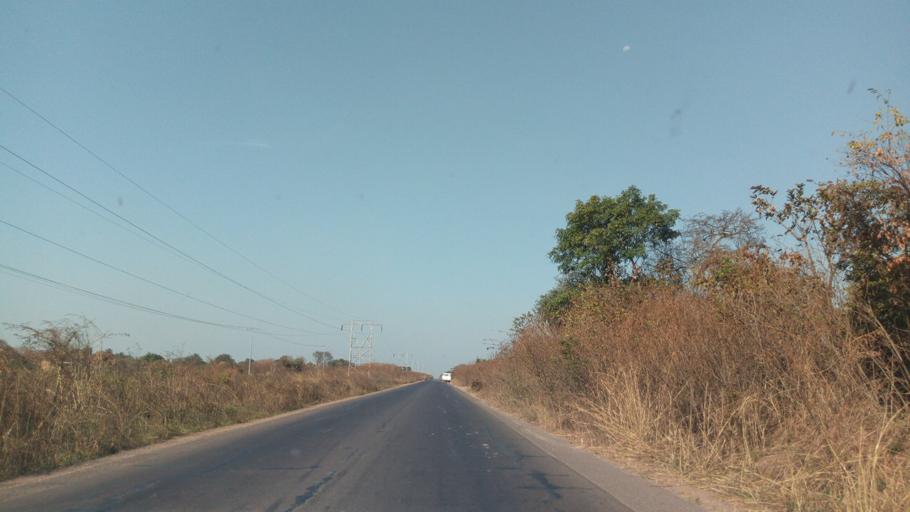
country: CD
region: Katanga
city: Likasi
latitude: -11.0020
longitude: 26.8615
